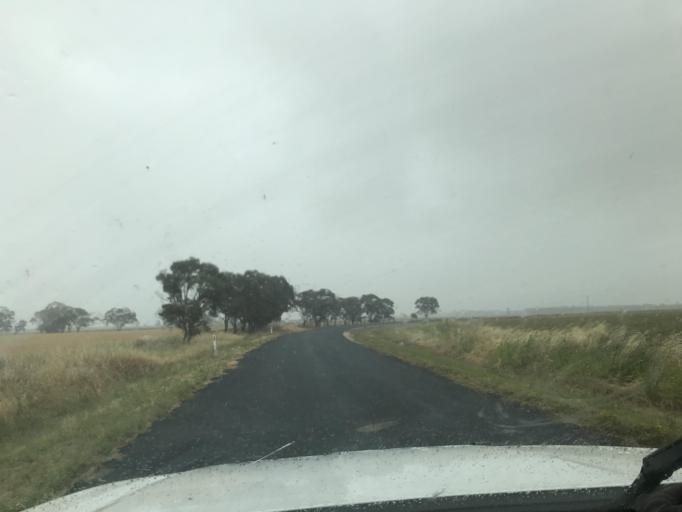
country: AU
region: South Australia
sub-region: Tatiara
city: Bordertown
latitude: -36.3133
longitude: 141.1470
